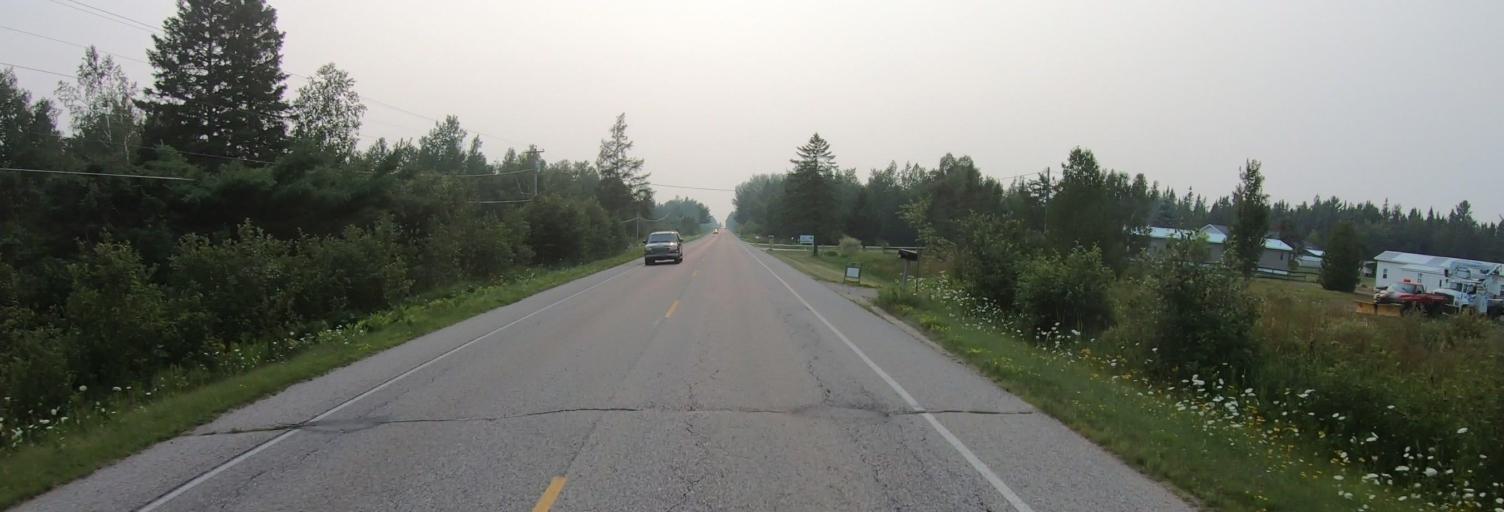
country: US
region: Michigan
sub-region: Chippewa County
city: Sault Ste. Marie
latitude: 46.4188
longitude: -84.4937
